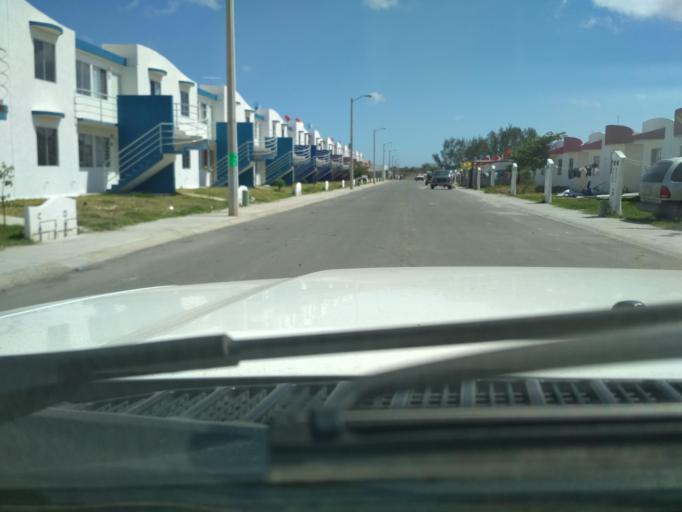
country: MX
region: Veracruz
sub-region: Veracruz
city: Las Amapolas
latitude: 19.1328
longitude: -96.2073
